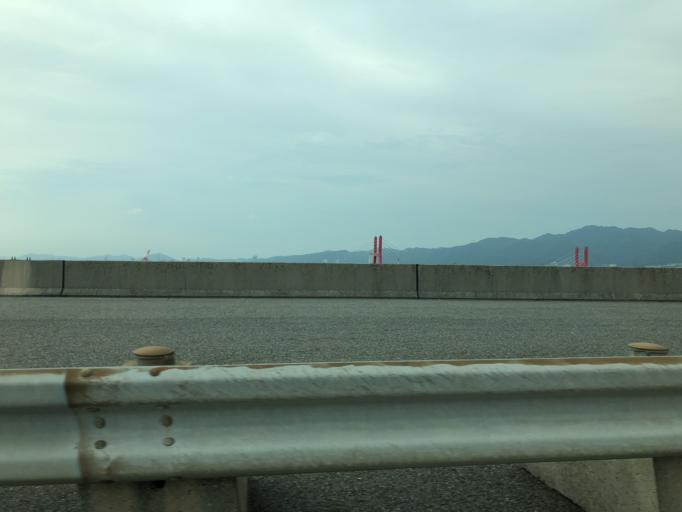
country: JP
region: Hyogo
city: Ashiya
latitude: 34.6980
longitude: 135.2733
